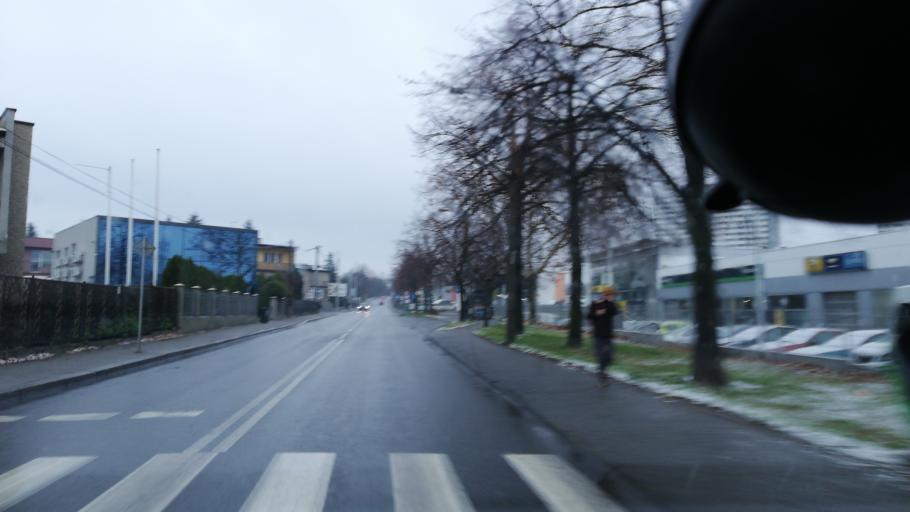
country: PL
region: Silesian Voivodeship
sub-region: Chorzow
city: Chorzow
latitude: 50.2844
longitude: 18.9621
